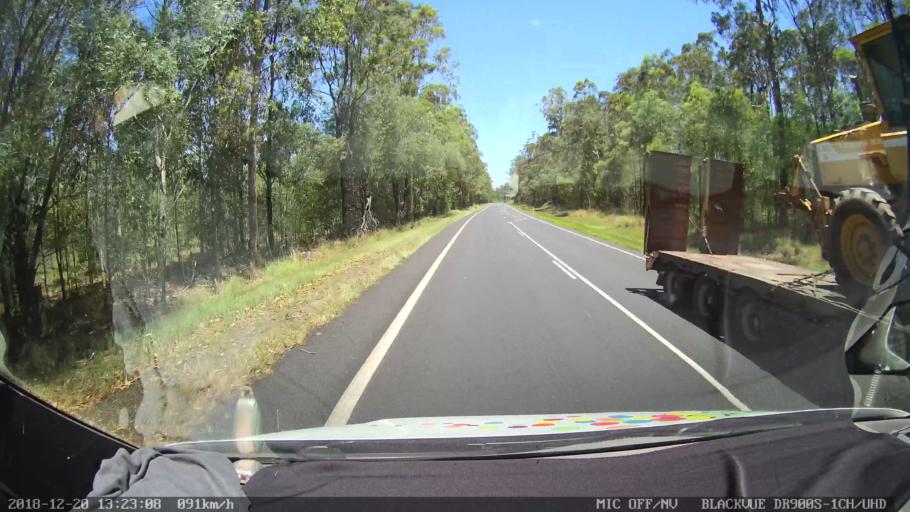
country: AU
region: New South Wales
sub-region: Richmond Valley
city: Casino
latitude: -29.1005
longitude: 153.0008
